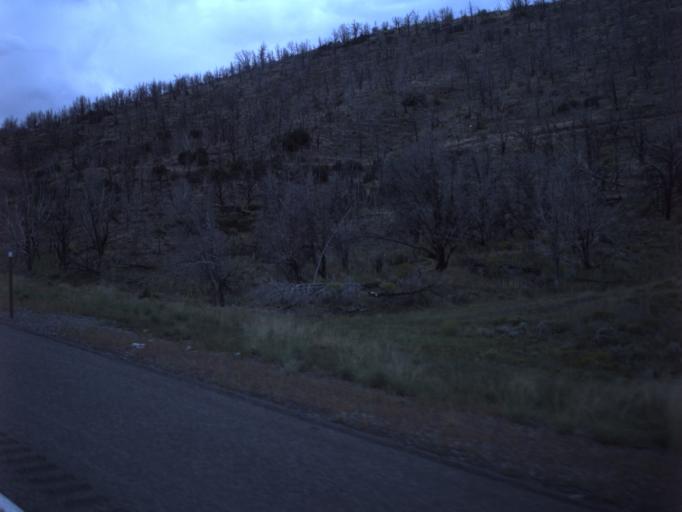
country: US
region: Utah
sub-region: Sevier County
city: Monroe
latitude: 38.5585
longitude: -112.4259
